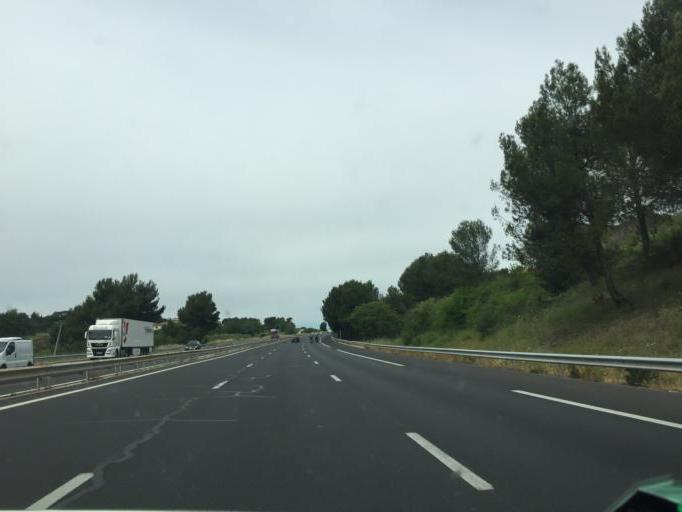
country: FR
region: Provence-Alpes-Cote d'Azur
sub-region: Departement des Bouches-du-Rhone
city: Aix-en-Provence
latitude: 43.5220
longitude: 5.4122
